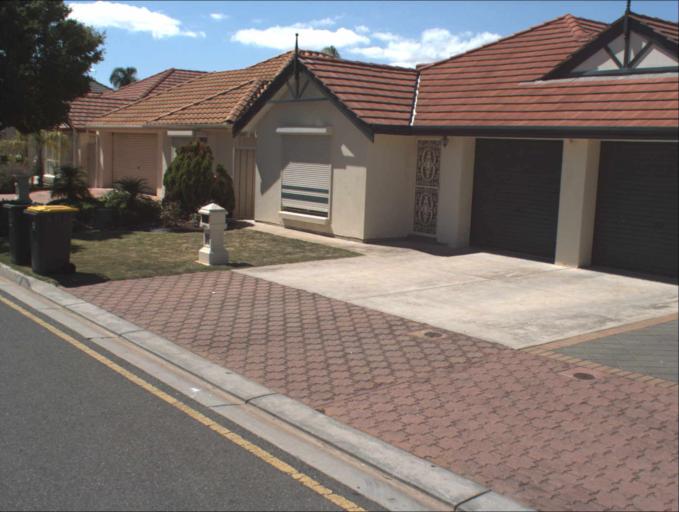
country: AU
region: South Australia
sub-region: Port Adelaide Enfield
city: Birkenhead
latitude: -34.8485
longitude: 138.4991
